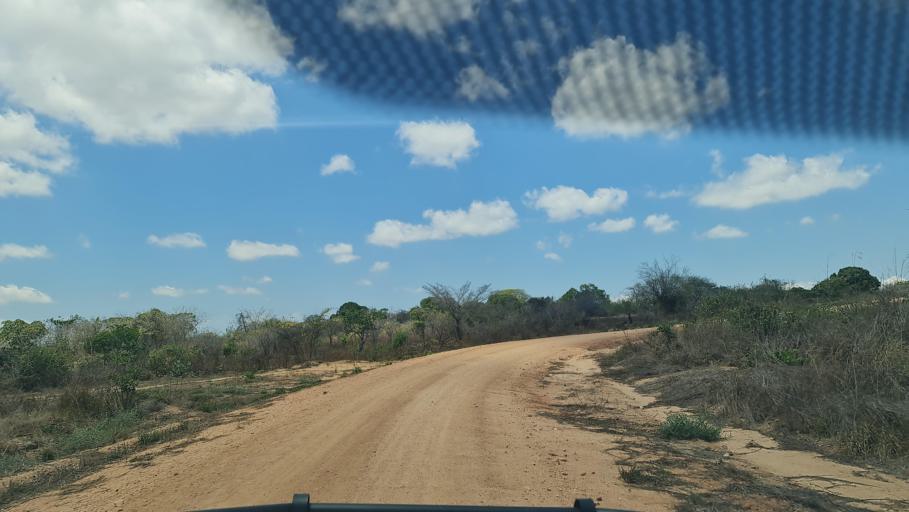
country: MZ
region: Nampula
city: Nacala
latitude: -14.3166
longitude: 40.5849
